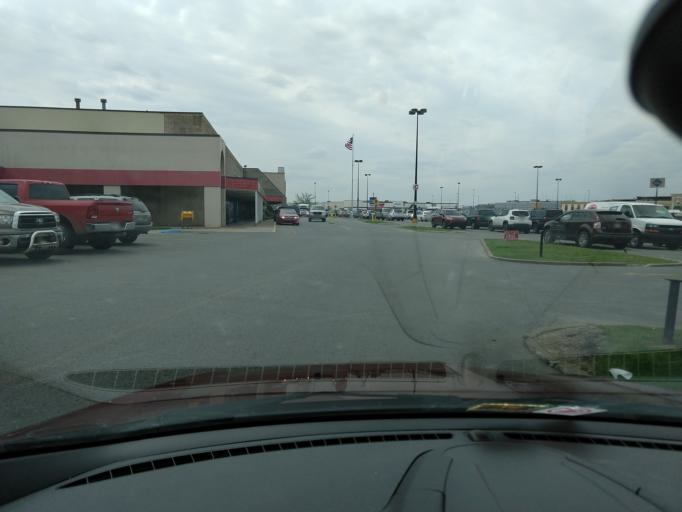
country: US
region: West Virginia
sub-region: Harrison County
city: Bridgeport
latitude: 39.2776
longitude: -80.2801
